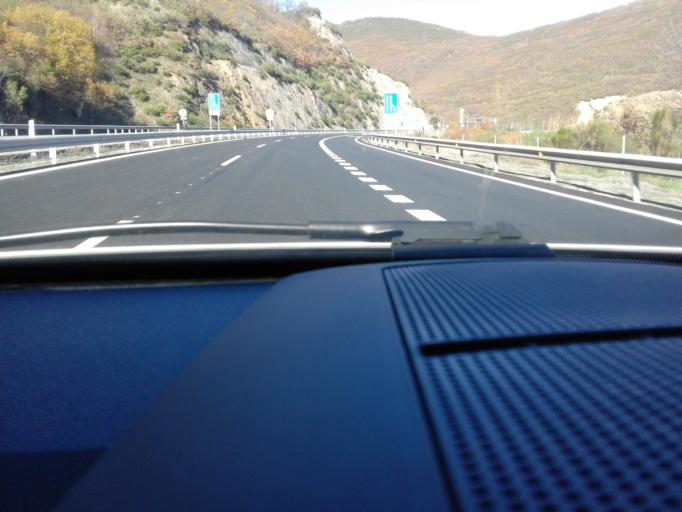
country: ES
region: Castille and Leon
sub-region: Provincia de Leon
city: Soto y Amio
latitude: 42.8408
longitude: -5.8748
